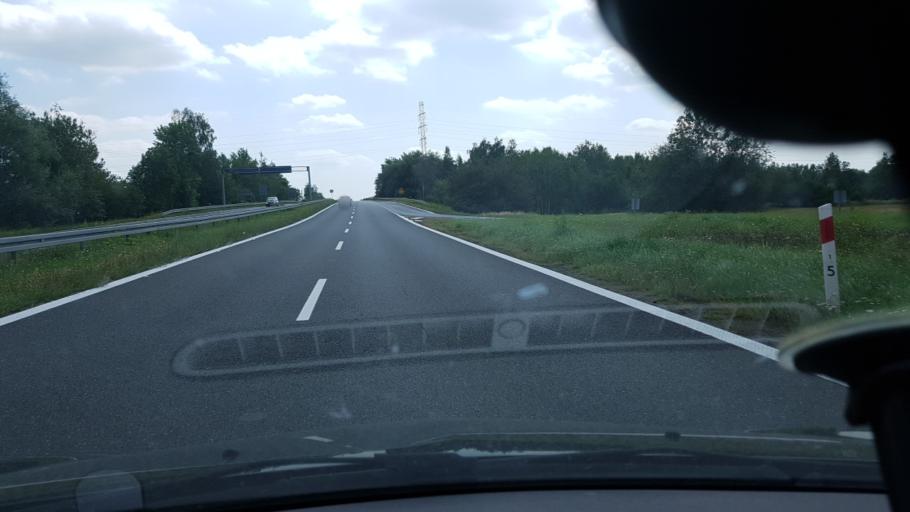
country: PL
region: Silesian Voivodeship
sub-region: Powiat bierunsko-ledzinski
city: Bierun
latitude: 50.1038
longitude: 19.0943
